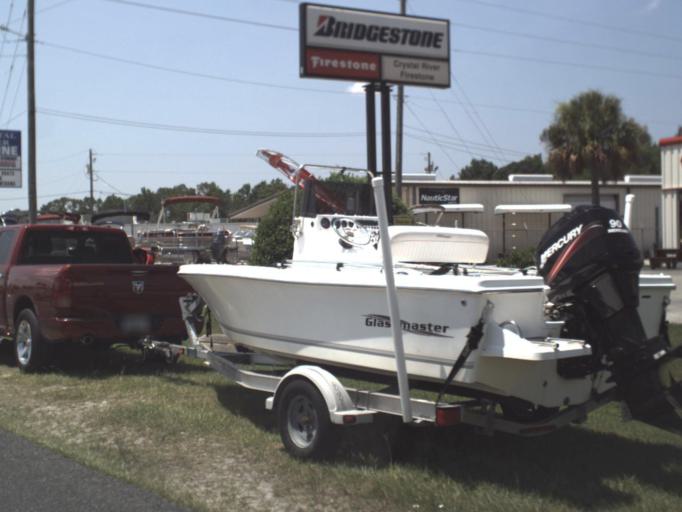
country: US
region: Florida
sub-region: Citrus County
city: Crystal River
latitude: 28.8769
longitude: -82.5805
